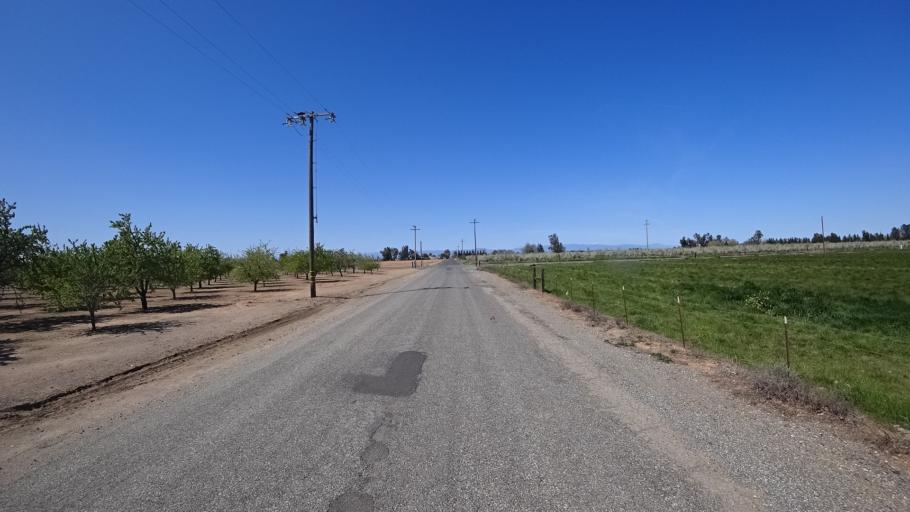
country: US
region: California
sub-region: Glenn County
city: Hamilton City
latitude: 39.7896
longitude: -122.0654
